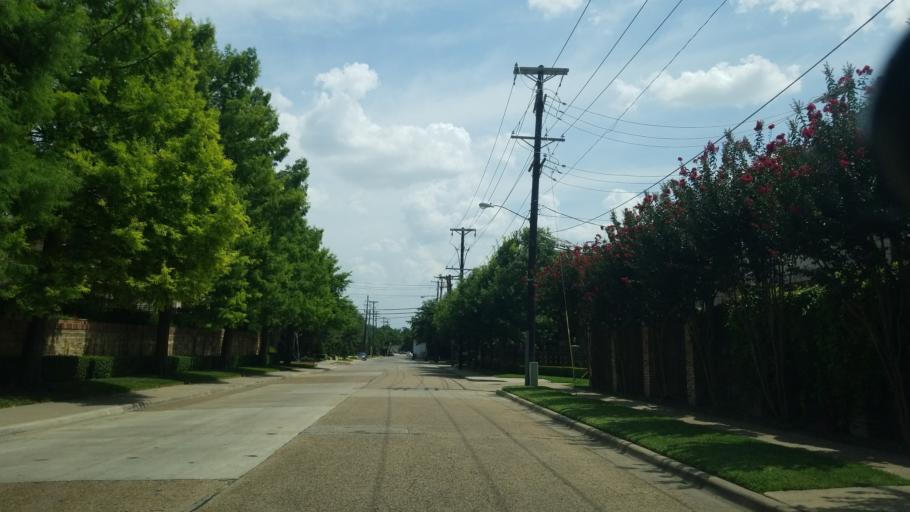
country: US
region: Texas
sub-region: Dallas County
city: University Park
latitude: 32.8686
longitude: -96.7896
